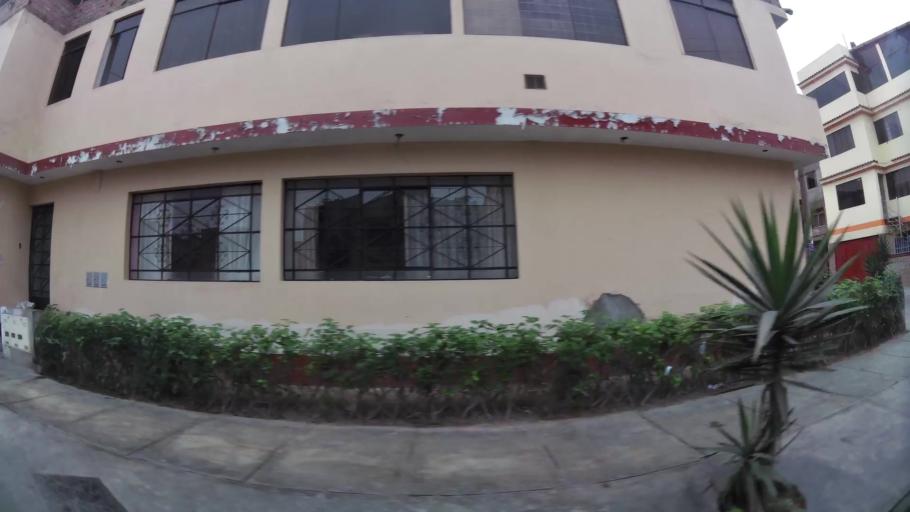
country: PE
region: Lima
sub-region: Lima
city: Surco
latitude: -12.1705
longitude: -76.9695
